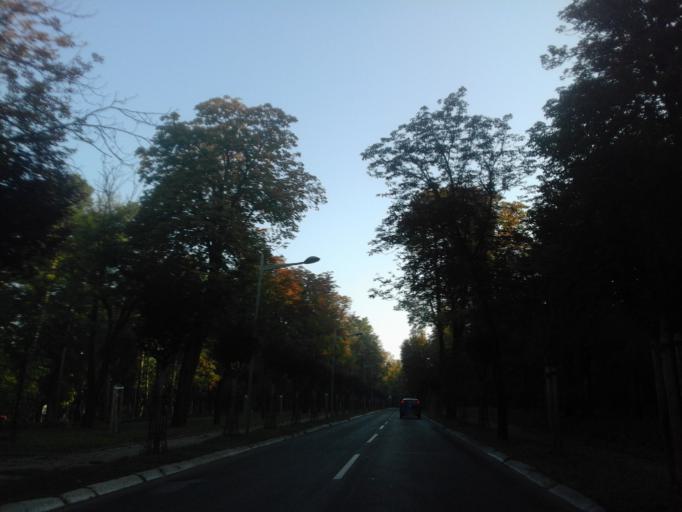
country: RS
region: Central Serbia
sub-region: Belgrade
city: Savski Venac
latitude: 44.7860
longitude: 20.4422
